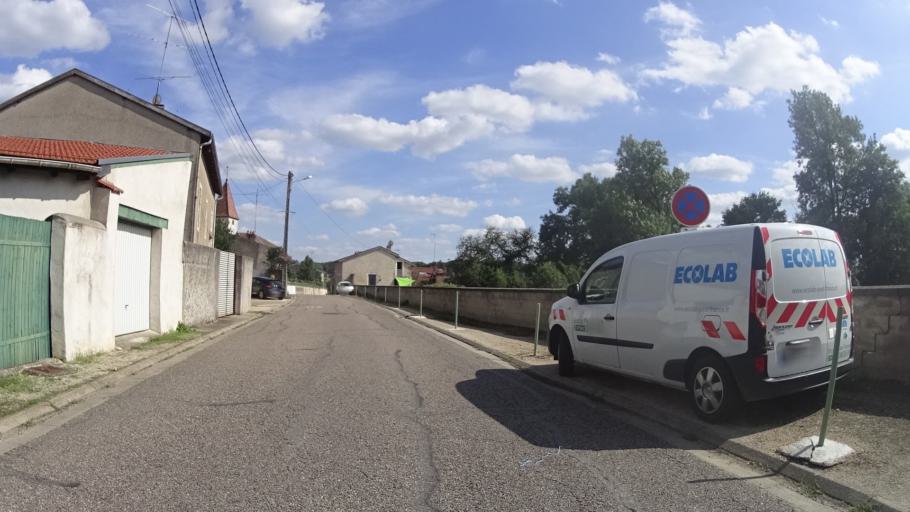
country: FR
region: Lorraine
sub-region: Departement de Meurthe-et-Moselle
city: Dommartin-les-Toul
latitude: 48.6532
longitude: 5.9049
